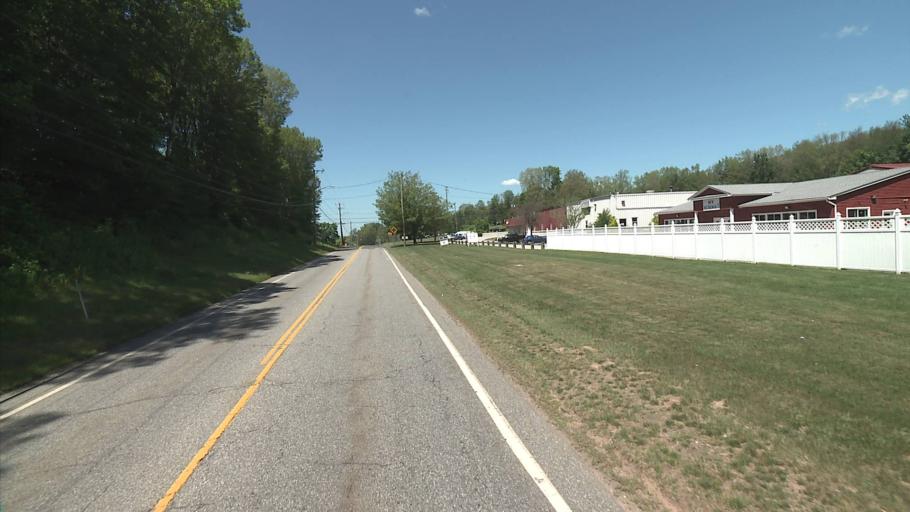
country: US
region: Connecticut
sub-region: Middlesex County
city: East Hampton
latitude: 41.5640
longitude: -72.5367
